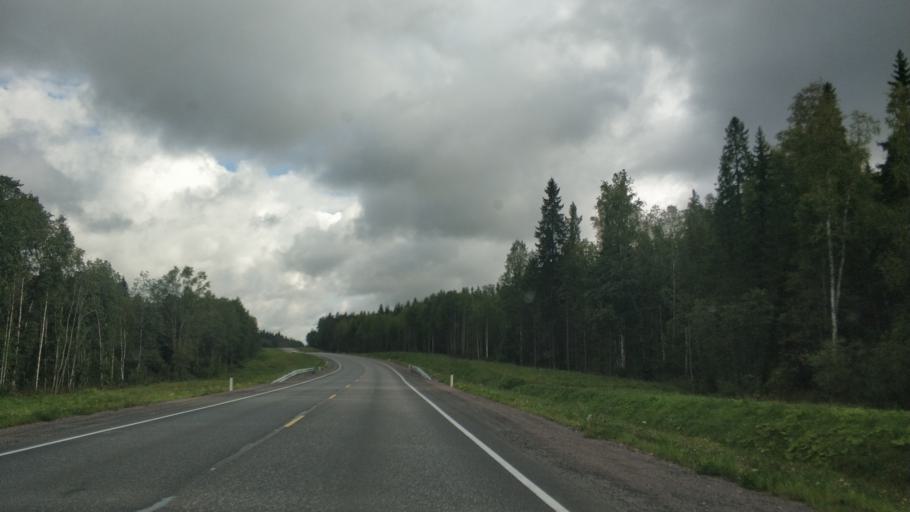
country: RU
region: Republic of Karelia
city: Ruskeala
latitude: 61.8547
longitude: 30.6513
